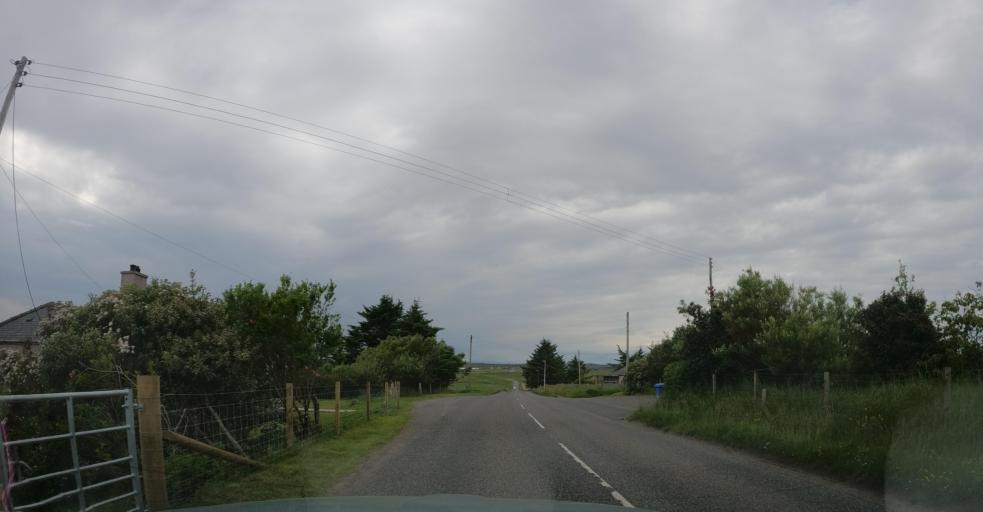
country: GB
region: Scotland
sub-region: Eilean Siar
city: Isle of Lewis
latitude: 58.2727
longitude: -6.3150
